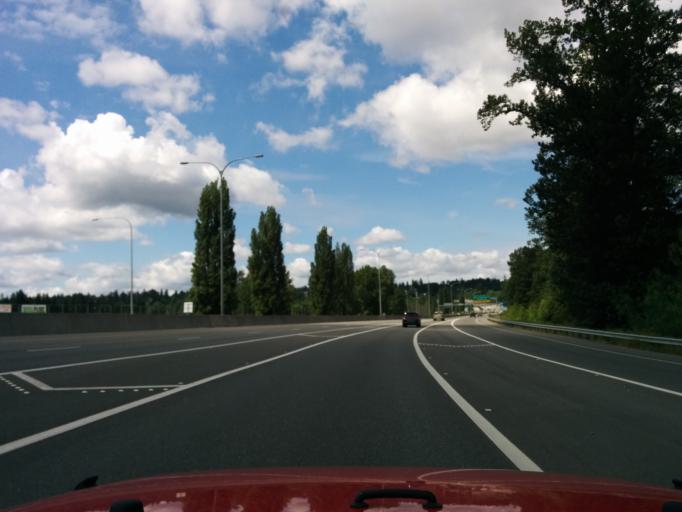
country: US
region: Washington
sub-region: King County
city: Redmond
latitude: 47.6675
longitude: -122.1120
